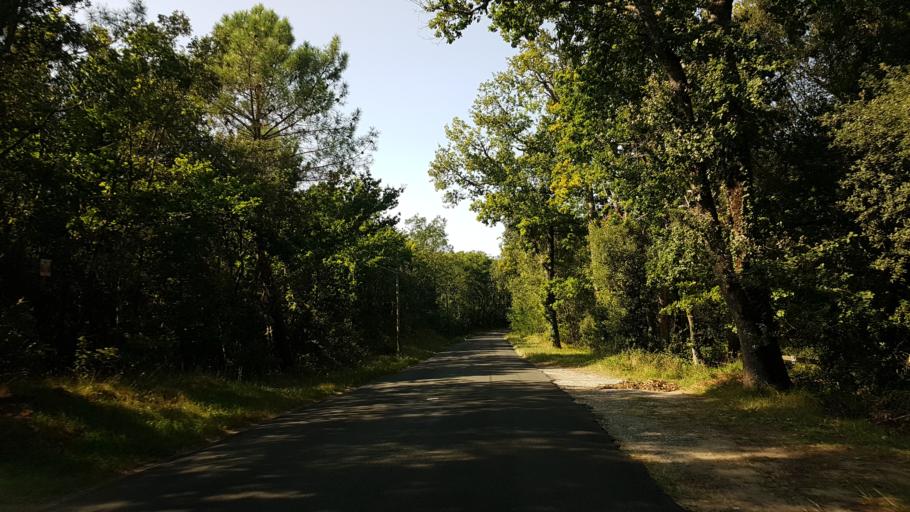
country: FR
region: Poitou-Charentes
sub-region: Departement de la Charente-Maritime
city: Saint-Palais-sur-Mer
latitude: 45.6635
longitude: -1.1197
